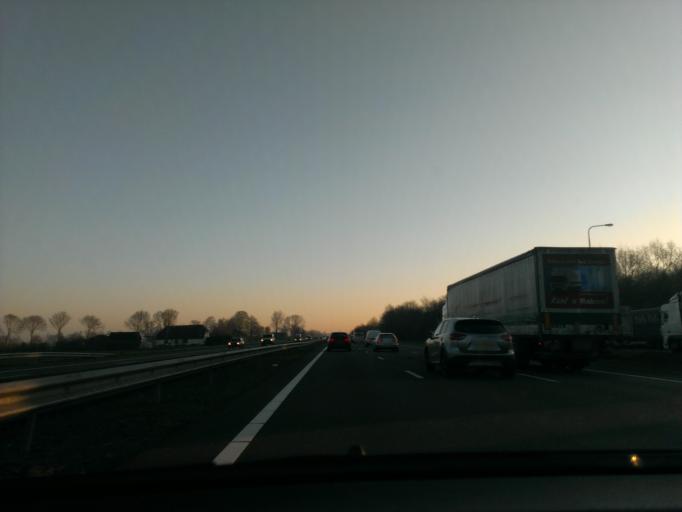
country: NL
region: Overijssel
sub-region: Gemeente Zwartewaterland
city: Hasselt
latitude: 52.5522
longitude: 6.1729
